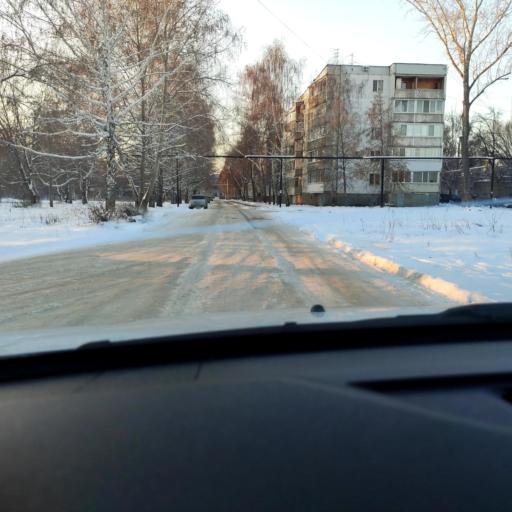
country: RU
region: Samara
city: Smyshlyayevka
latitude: 53.2510
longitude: 50.3770
